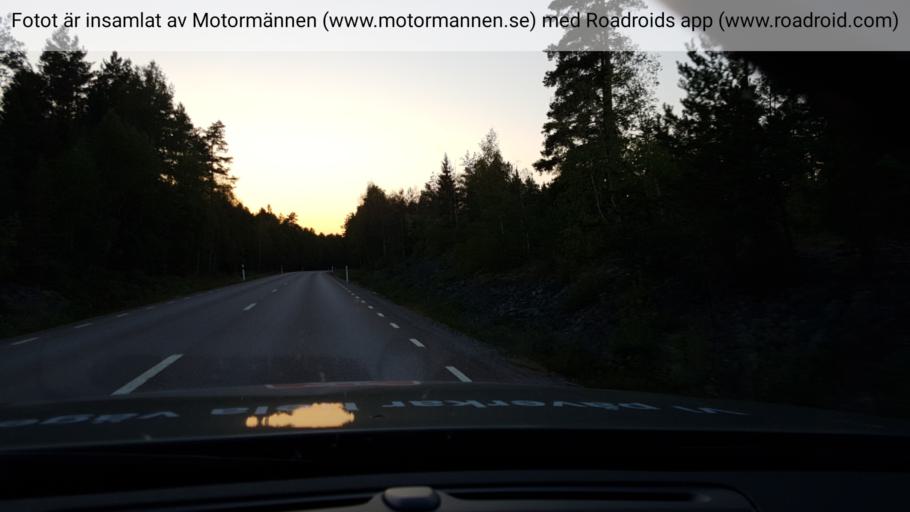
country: SE
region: Uppsala
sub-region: Heby Kommun
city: OEstervala
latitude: 60.0497
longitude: 17.2343
